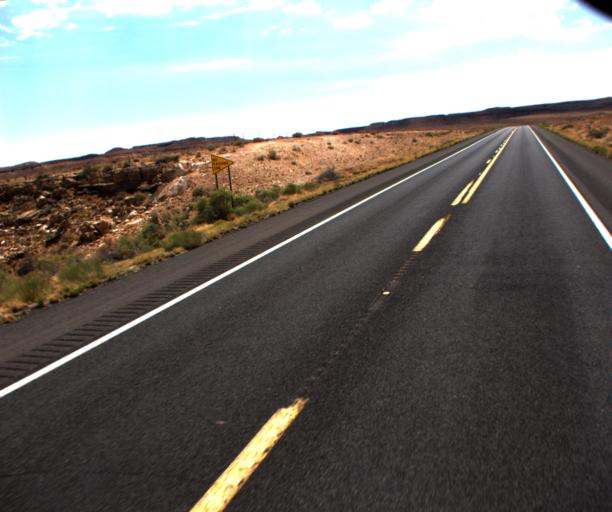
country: US
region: Arizona
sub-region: Coconino County
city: Tuba City
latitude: 35.8812
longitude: -111.5230
